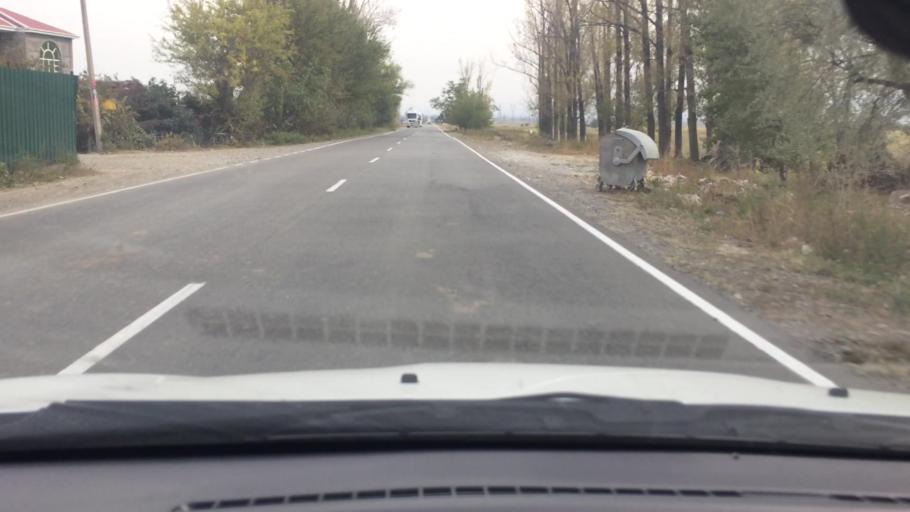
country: GE
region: Kvemo Kartli
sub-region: Gardabani
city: Gardabani
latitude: 41.4459
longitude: 44.9969
